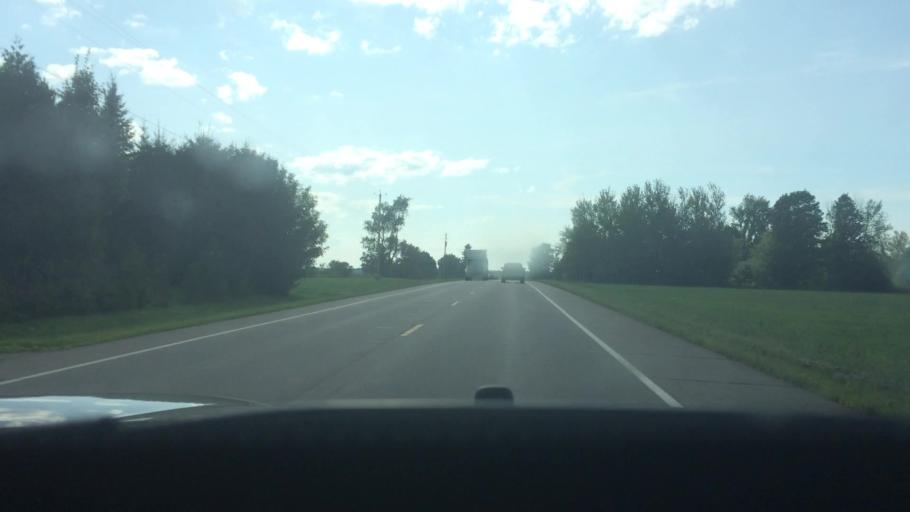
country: US
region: New York
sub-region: Franklin County
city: Malone
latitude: 44.8453
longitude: -74.1763
